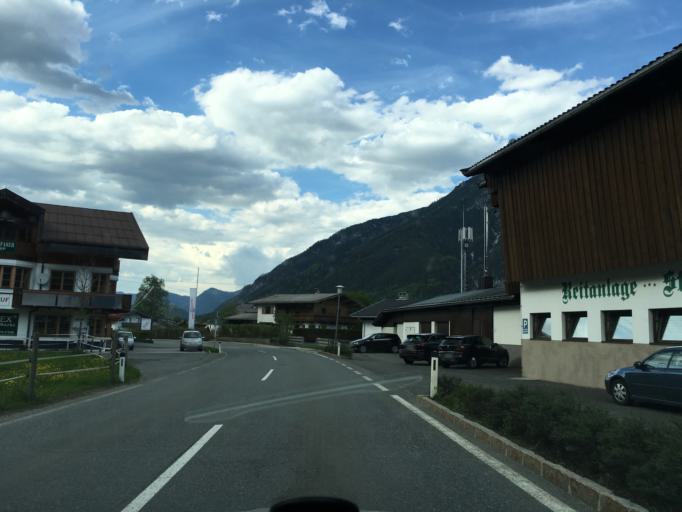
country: AT
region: Tyrol
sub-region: Politischer Bezirk Kitzbuhel
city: Fieberbrunn
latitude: 47.5123
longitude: 12.5801
